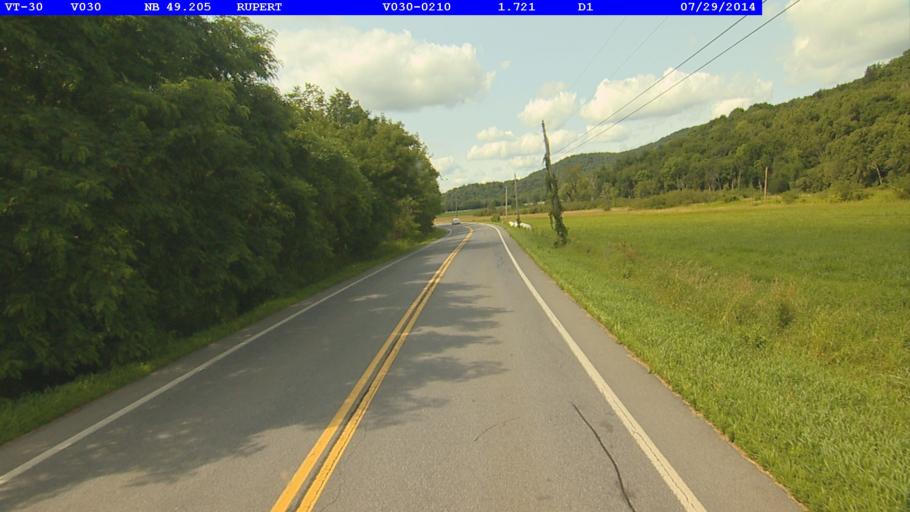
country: US
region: Vermont
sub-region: Bennington County
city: Manchester Center
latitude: 43.2917
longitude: -73.1390
